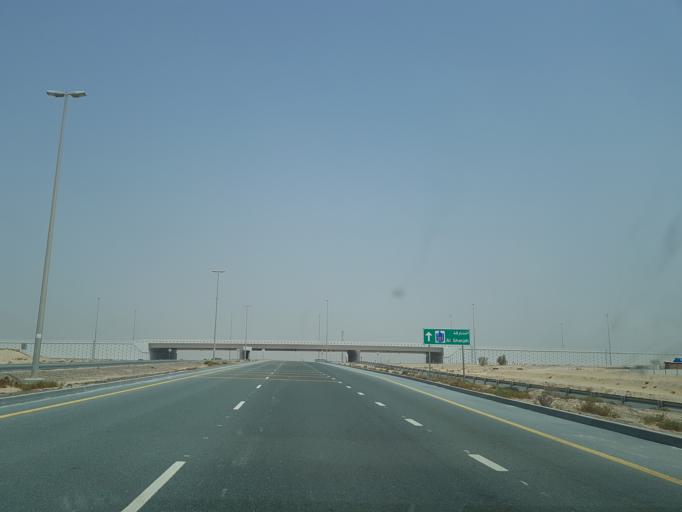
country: AE
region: Dubai
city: Dubai
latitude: 25.0561
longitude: 55.3031
